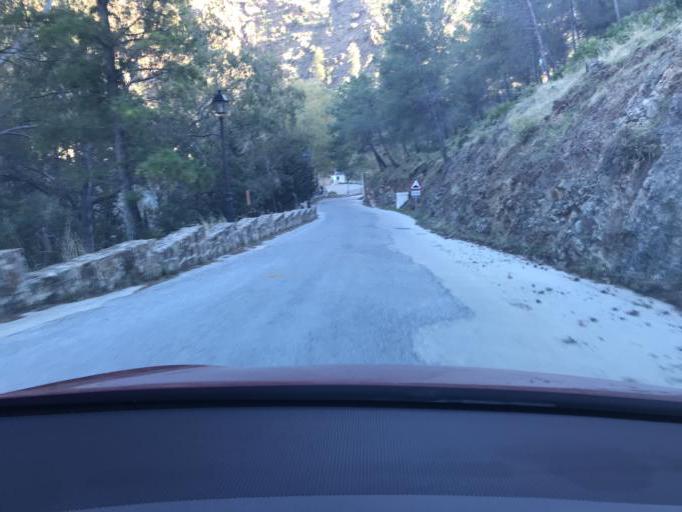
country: ES
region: Andalusia
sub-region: Provincia de Malaga
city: Tolox
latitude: 36.6807
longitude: -4.9093
